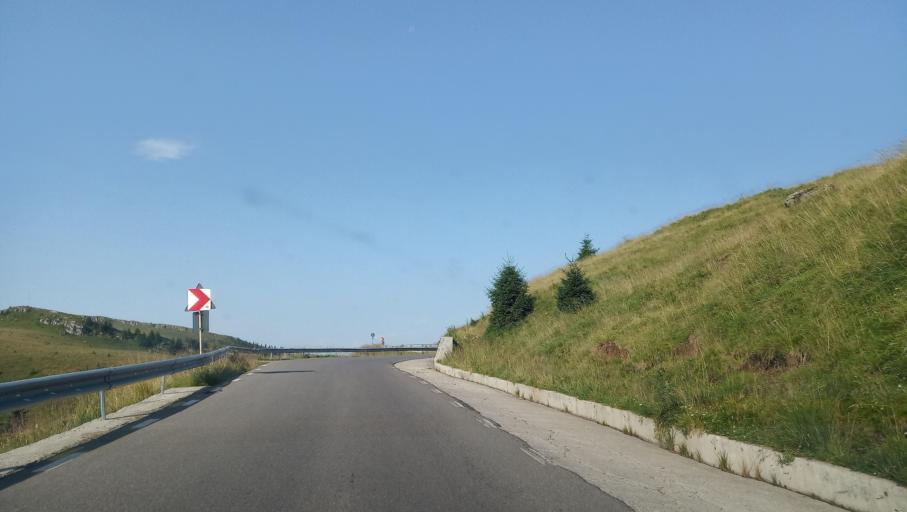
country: RO
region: Prahova
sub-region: Oras Sinaia
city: Sinaia
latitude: 45.3278
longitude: 25.4655
